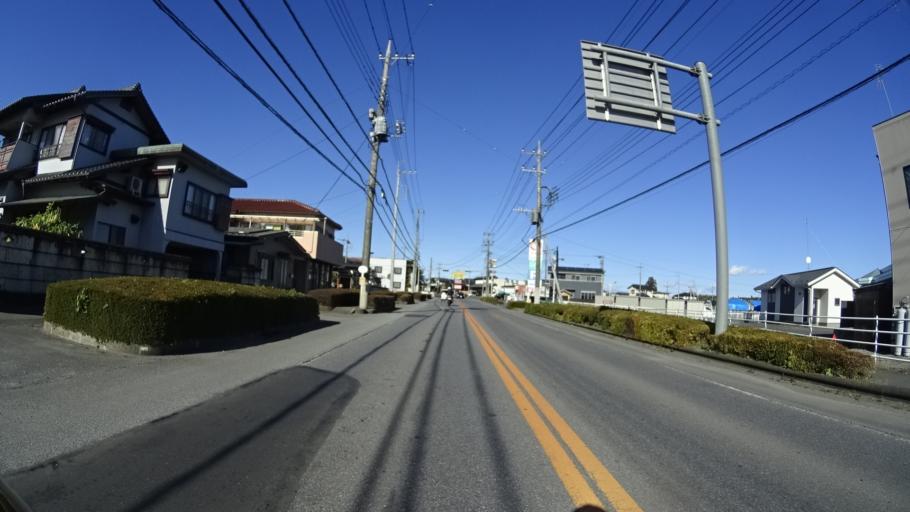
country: JP
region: Tochigi
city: Kanuma
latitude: 36.5154
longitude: 139.7517
